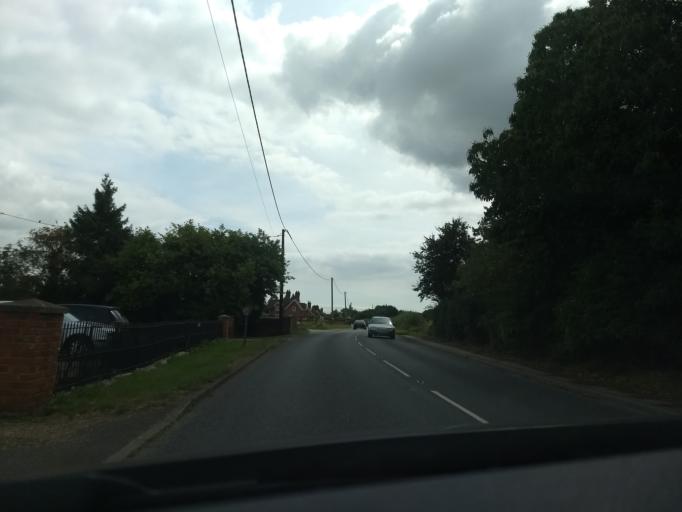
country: GB
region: England
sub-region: Suffolk
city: Ipswich
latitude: 52.0043
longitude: 1.1720
